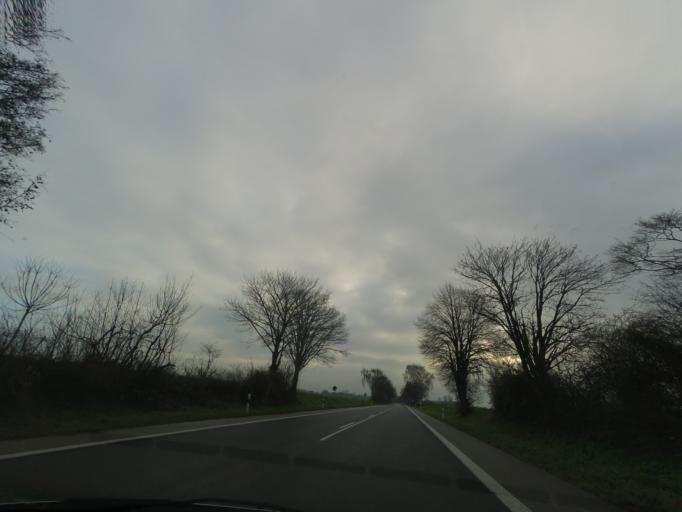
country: DE
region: North Rhine-Westphalia
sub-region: Regierungsbezirk Dusseldorf
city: Neubrueck
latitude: 51.1481
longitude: 6.5989
